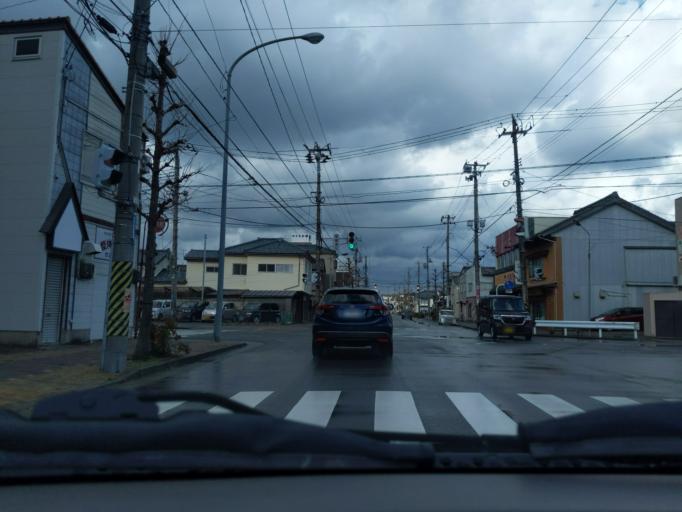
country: JP
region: Niigata
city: Niigata-shi
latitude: 37.9284
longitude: 139.0471
